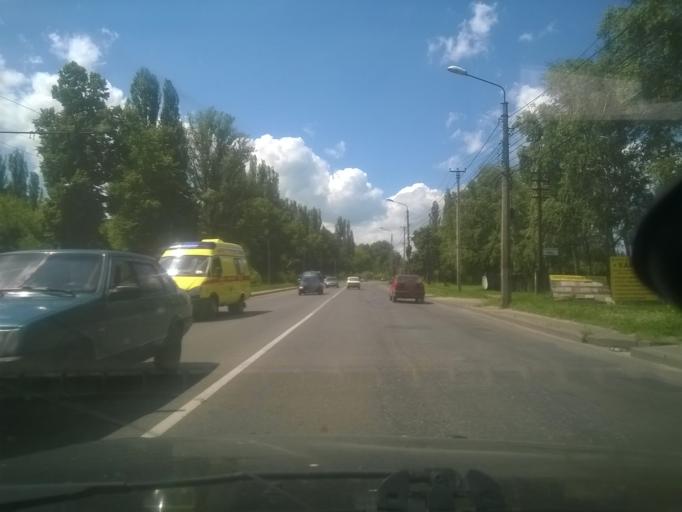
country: RU
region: Kursk
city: Kursk
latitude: 51.6618
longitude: 36.1296
